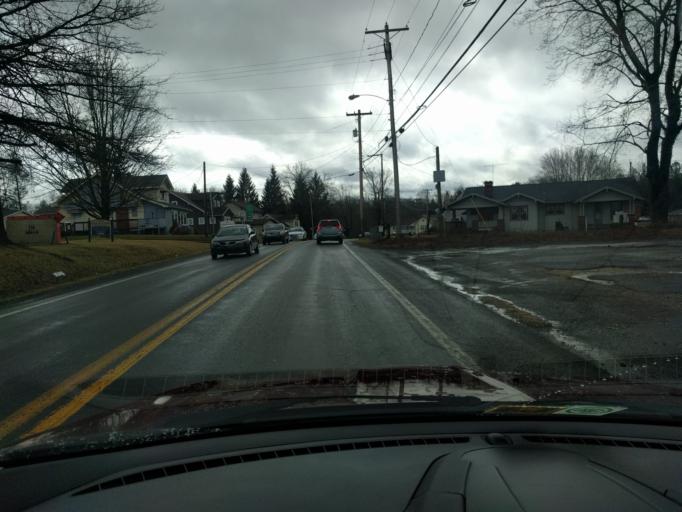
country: US
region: West Virginia
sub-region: Raleigh County
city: Mabscott
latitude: 37.7854
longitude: -81.2031
